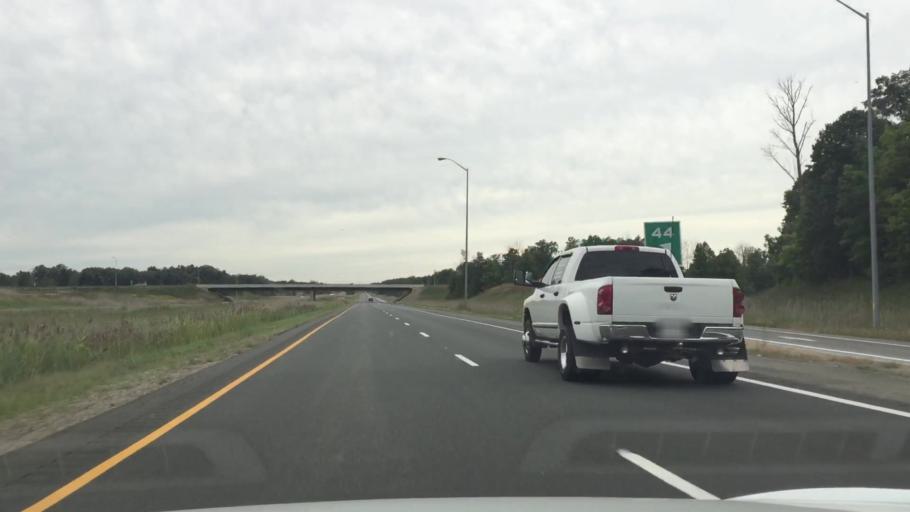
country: CA
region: Ontario
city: Lambton Shores
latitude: 42.9922
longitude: -81.8748
